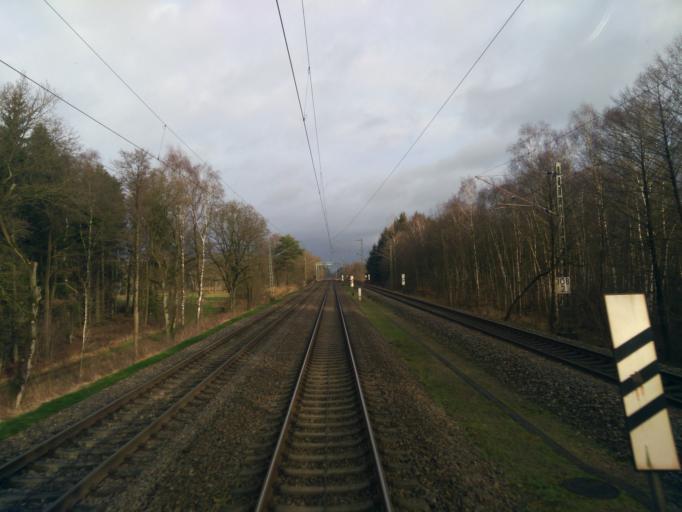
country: DE
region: Lower Saxony
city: Wistedt
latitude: 53.2529
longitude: 9.6904
